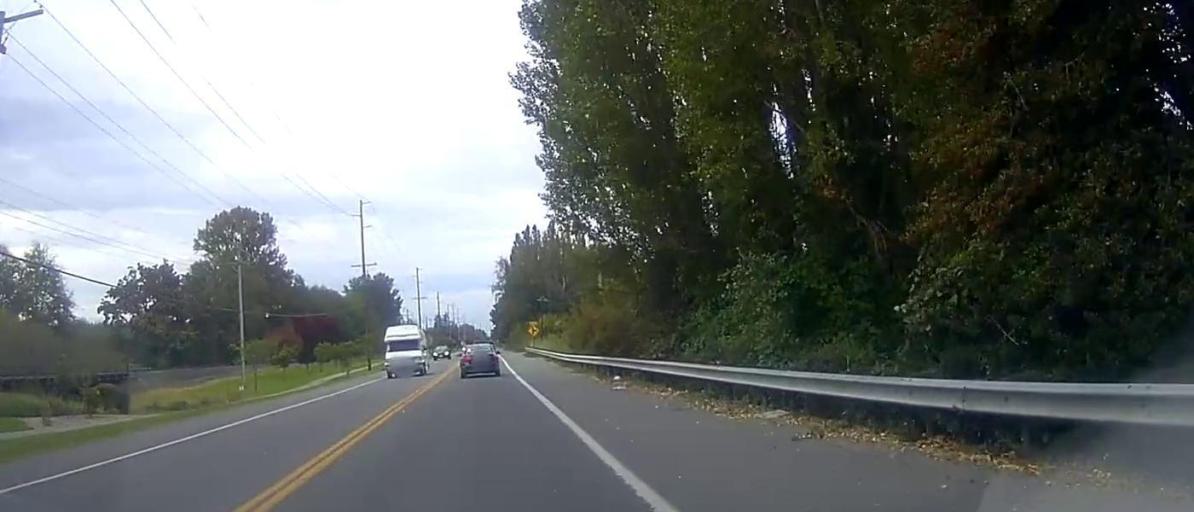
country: US
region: Washington
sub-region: Skagit County
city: Burlington
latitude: 48.4866
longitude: -122.2966
